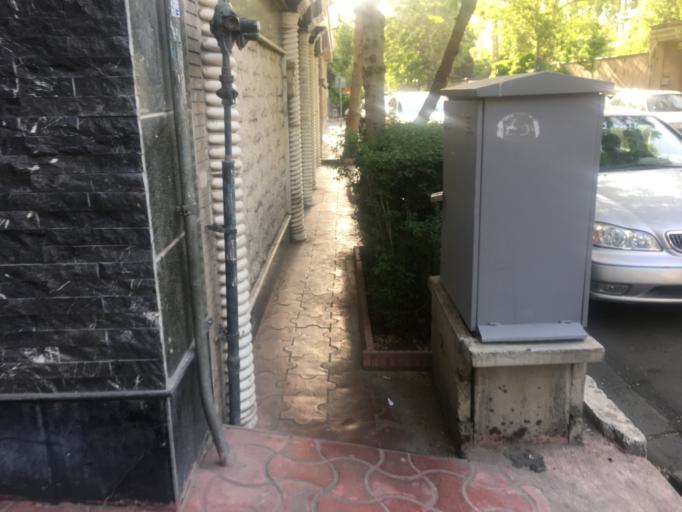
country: IR
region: Tehran
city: Tajrish
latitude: 35.7962
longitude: 51.4746
